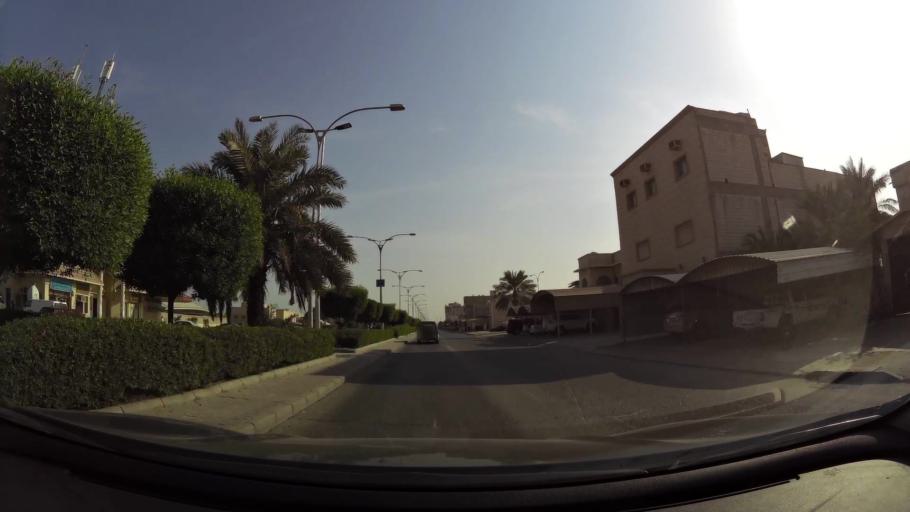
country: KW
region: Al Ahmadi
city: Ar Riqqah
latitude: 29.1406
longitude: 48.1078
